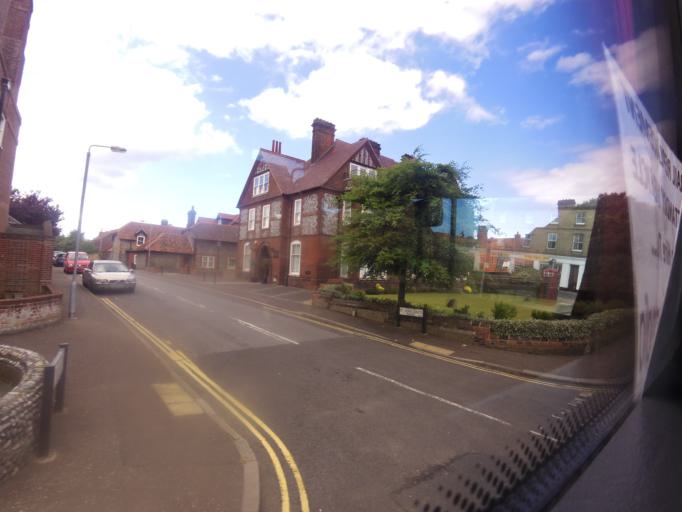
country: GB
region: England
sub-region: Norfolk
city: Cromer
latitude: 52.9292
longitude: 1.3031
